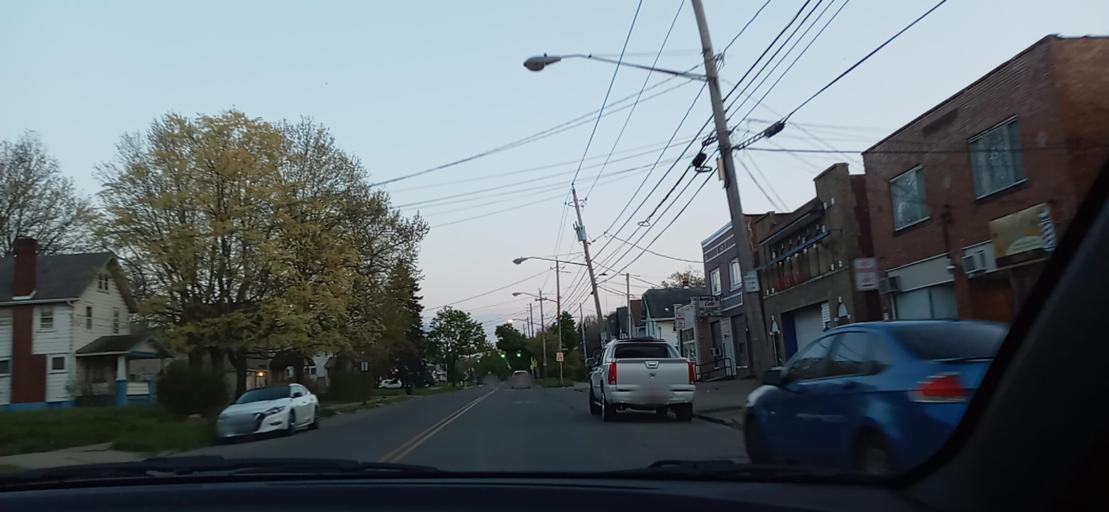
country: US
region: Ohio
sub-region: Summit County
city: Akron
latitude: 41.0525
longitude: -81.5101
